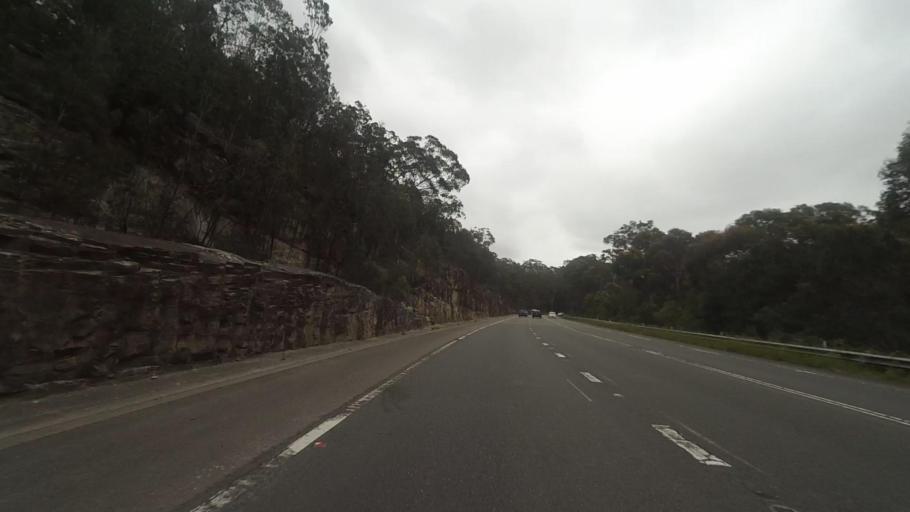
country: AU
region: New South Wales
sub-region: Sutherland Shire
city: Engadine
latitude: -34.0586
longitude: 150.9872
